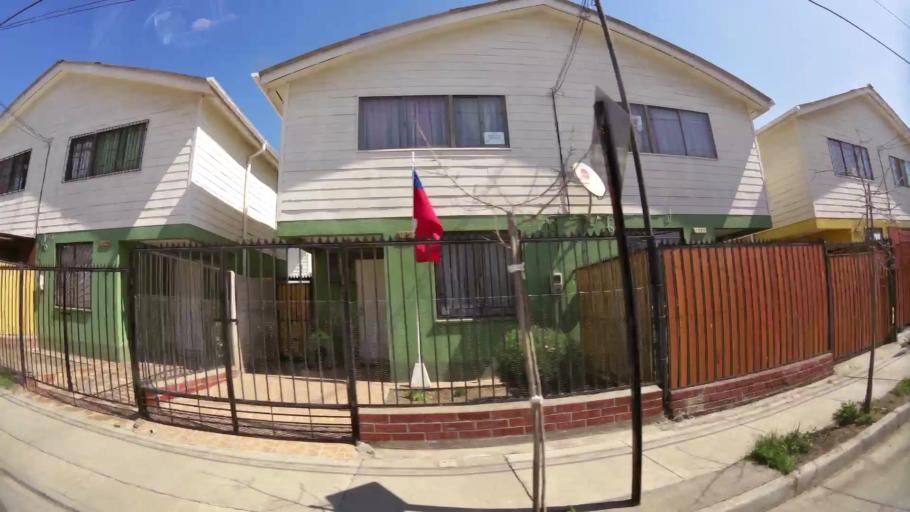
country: CL
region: Santiago Metropolitan
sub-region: Provincia de Talagante
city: Penaflor
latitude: -33.5746
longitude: -70.8039
